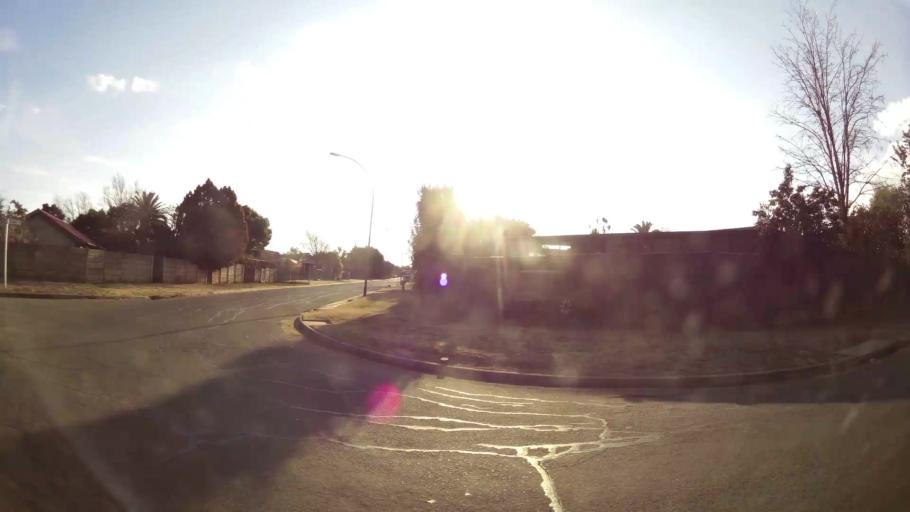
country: ZA
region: Orange Free State
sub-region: Mangaung Metropolitan Municipality
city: Bloemfontein
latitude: -29.1609
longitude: 26.1835
